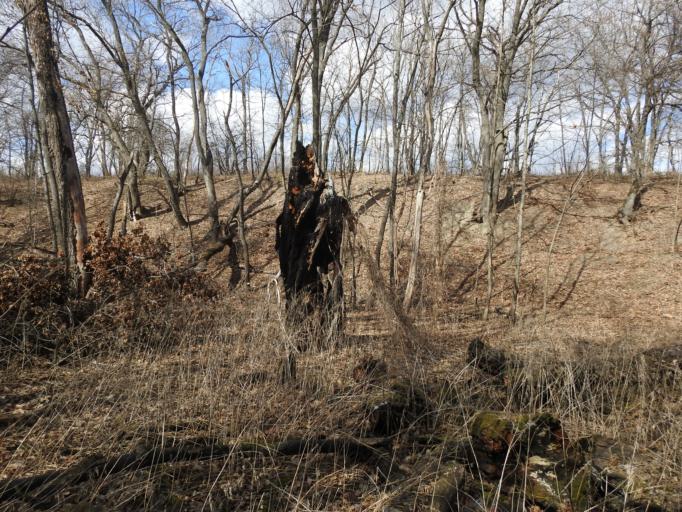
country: RU
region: Saratov
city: Krasnyy Oktyabr'
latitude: 51.3831
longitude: 45.7728
